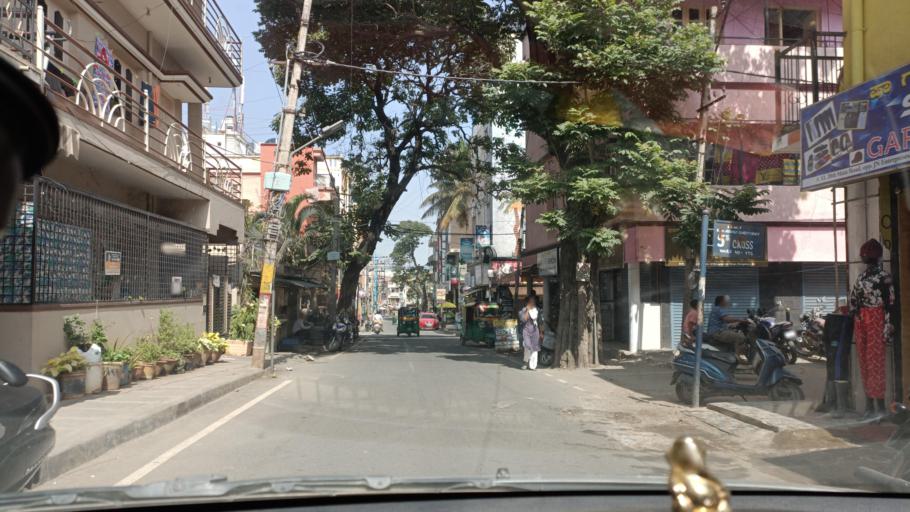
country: IN
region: Karnataka
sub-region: Bangalore Urban
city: Bangalore
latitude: 12.9184
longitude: 77.6127
